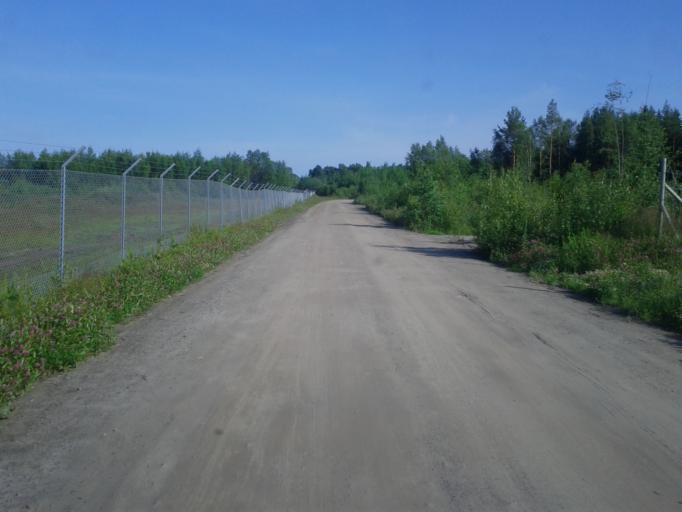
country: SE
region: Vaesterbotten
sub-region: Umea Kommun
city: Umea
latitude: 63.7810
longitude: 20.2977
